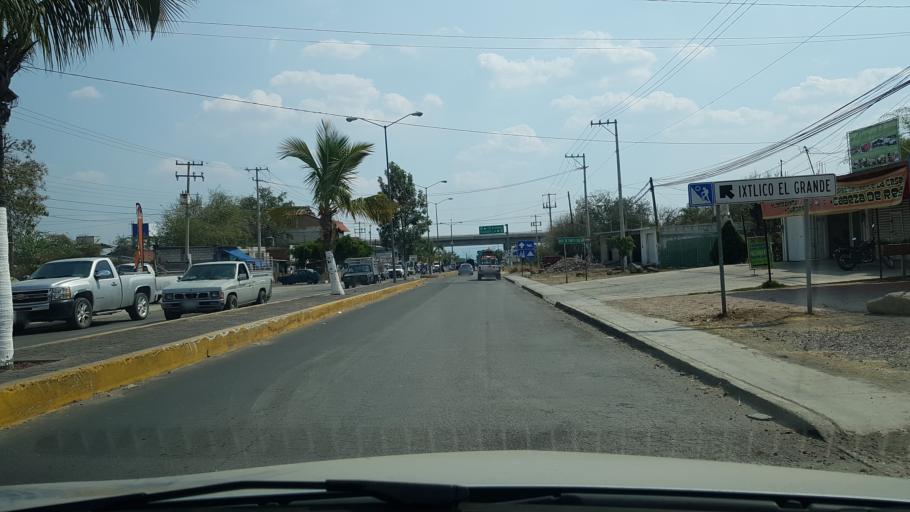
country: MX
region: Morelos
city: Amayuca
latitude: 18.7193
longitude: -98.7945
